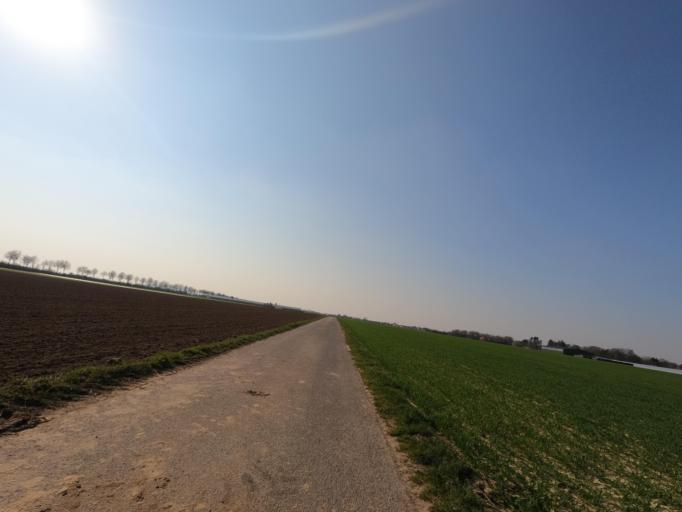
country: DE
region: North Rhine-Westphalia
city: Huckelhoven
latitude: 51.0944
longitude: 6.2620
